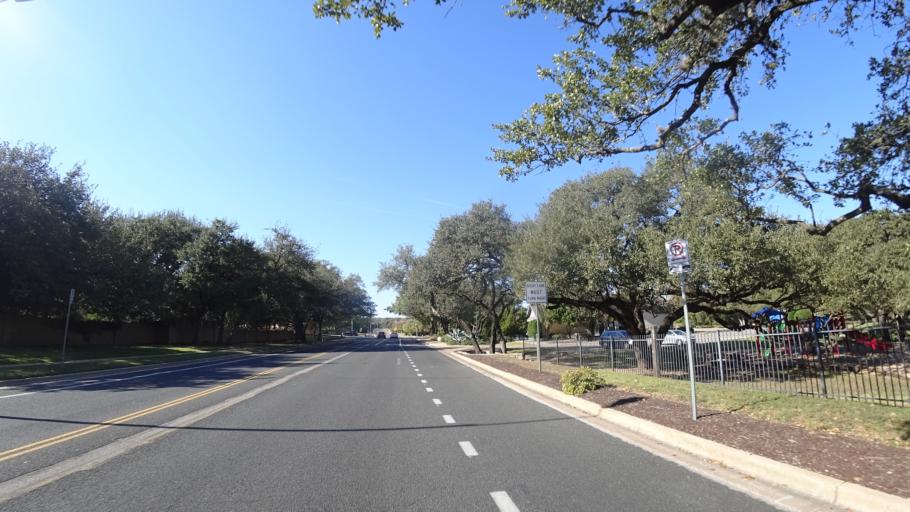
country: US
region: Texas
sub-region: Travis County
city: Barton Creek
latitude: 30.2252
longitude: -97.8675
